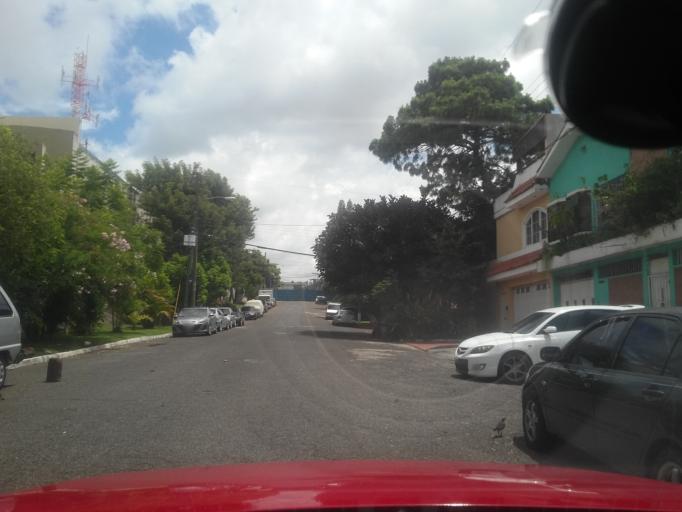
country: GT
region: Guatemala
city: Mixco
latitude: 14.6442
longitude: -90.5655
